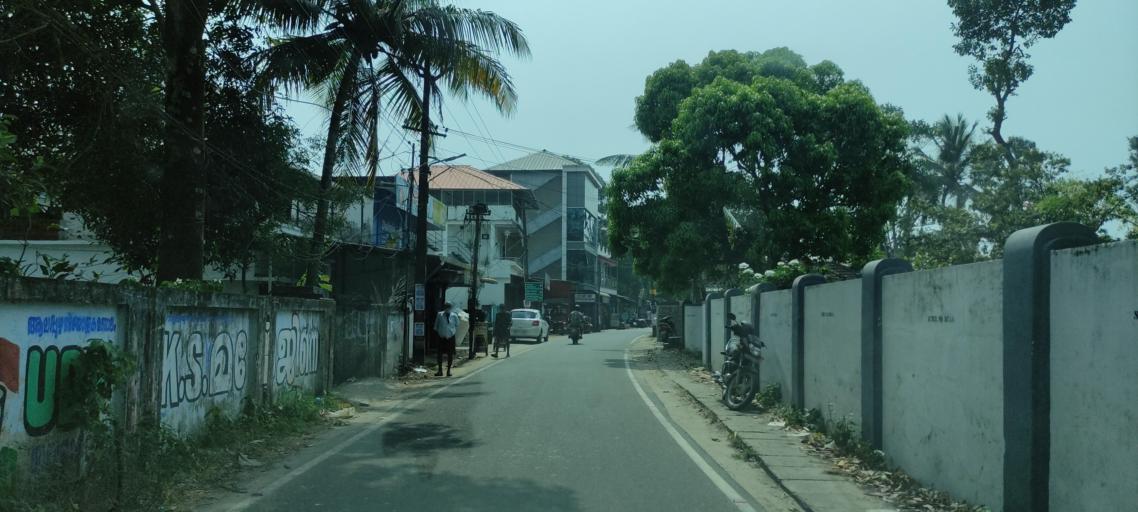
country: IN
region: Kerala
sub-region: Alappuzha
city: Alleppey
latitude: 9.5054
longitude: 76.3339
